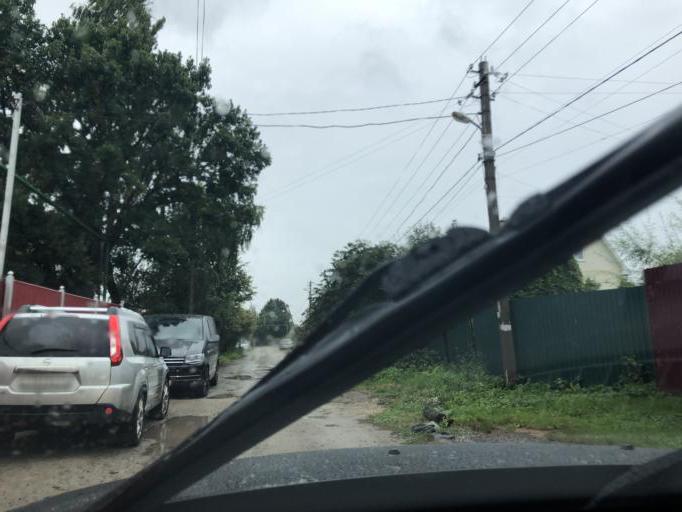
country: RU
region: Tula
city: Gorelki
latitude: 54.2593
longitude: 37.6195
